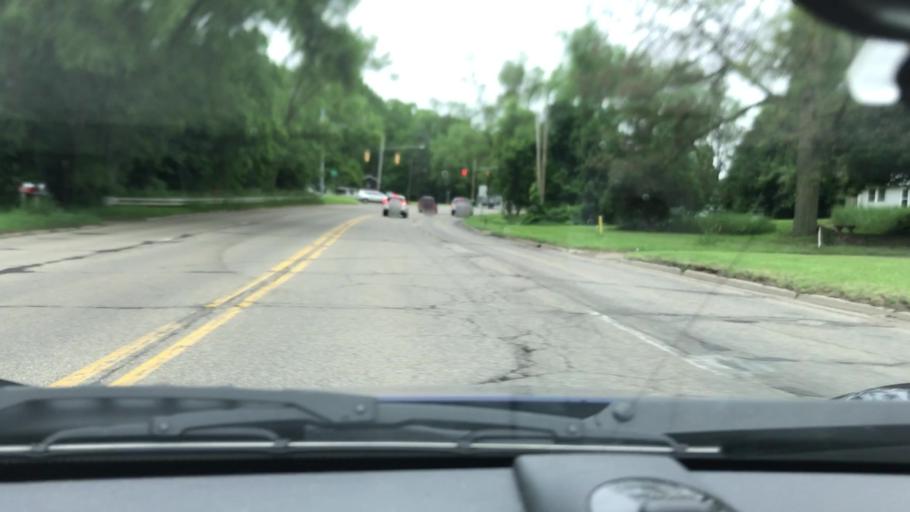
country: US
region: Michigan
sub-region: Calhoun County
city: Springfield
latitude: 42.3555
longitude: -85.2314
